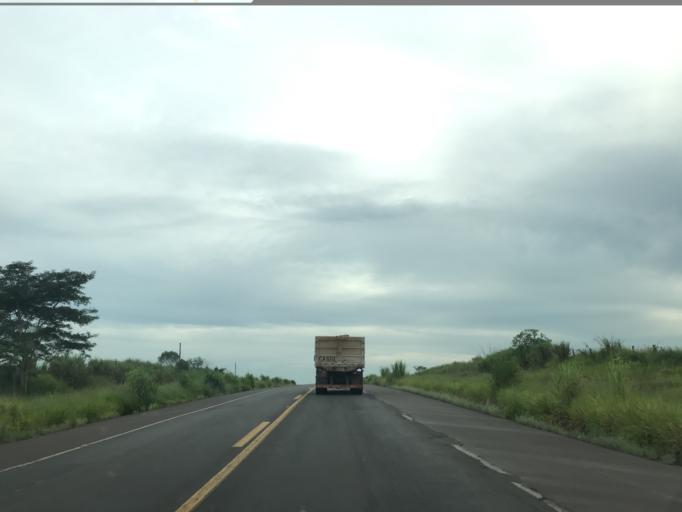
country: BR
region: Sao Paulo
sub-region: Tupa
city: Tupa
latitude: -21.6533
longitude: -50.5288
